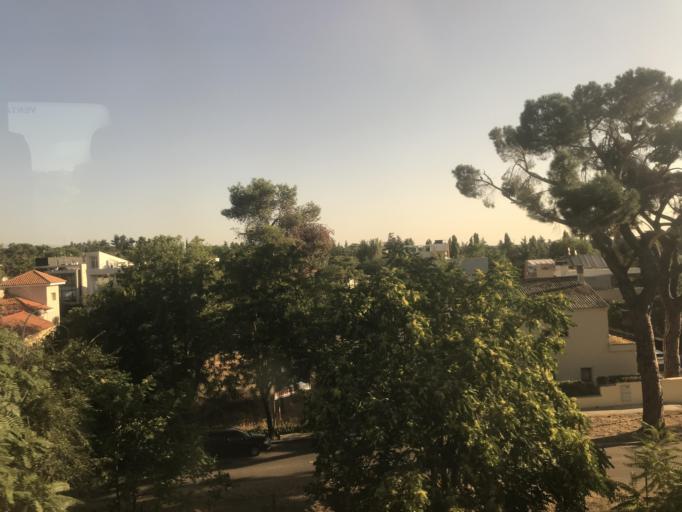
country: ES
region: Madrid
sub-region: Provincia de Madrid
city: Majadahonda
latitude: 40.4722
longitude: -3.8325
